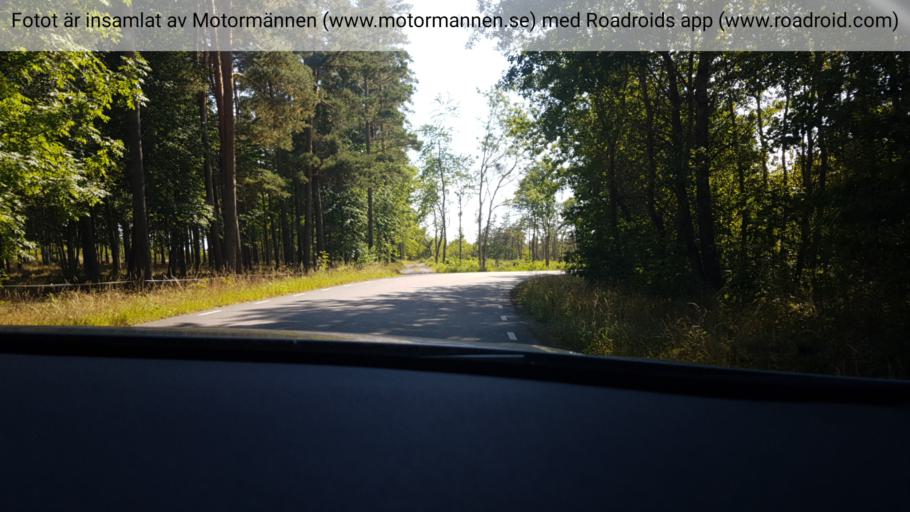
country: SE
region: Vaestra Goetaland
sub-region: Gotene Kommun
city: Kallby
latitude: 58.5282
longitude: 13.3227
